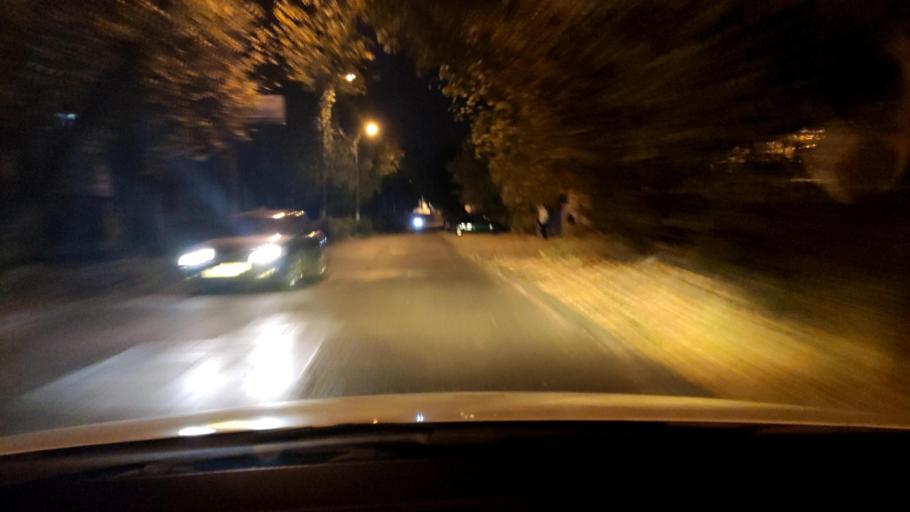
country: RU
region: Voronezj
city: Voronezh
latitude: 51.6613
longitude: 39.1341
